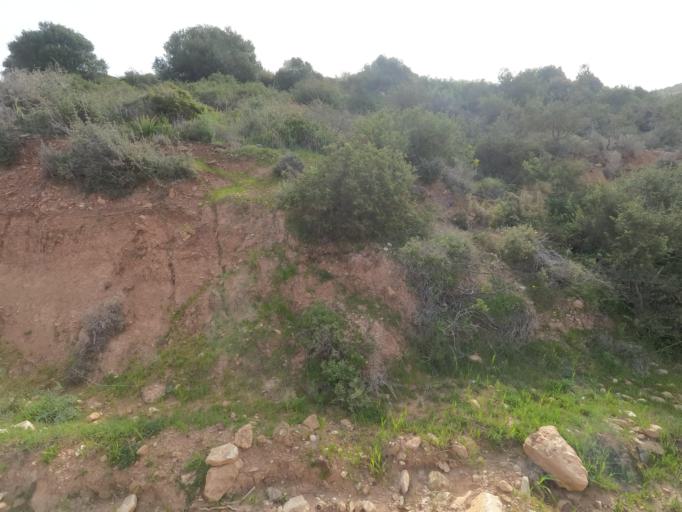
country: CY
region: Pafos
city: Pegeia
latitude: 34.9490
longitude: 32.3644
